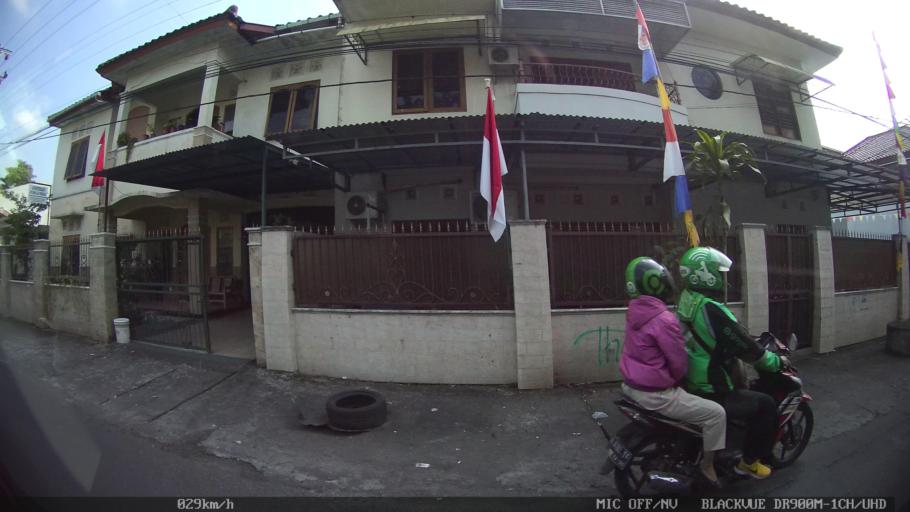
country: ID
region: Daerah Istimewa Yogyakarta
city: Melati
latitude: -7.7562
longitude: 110.3925
